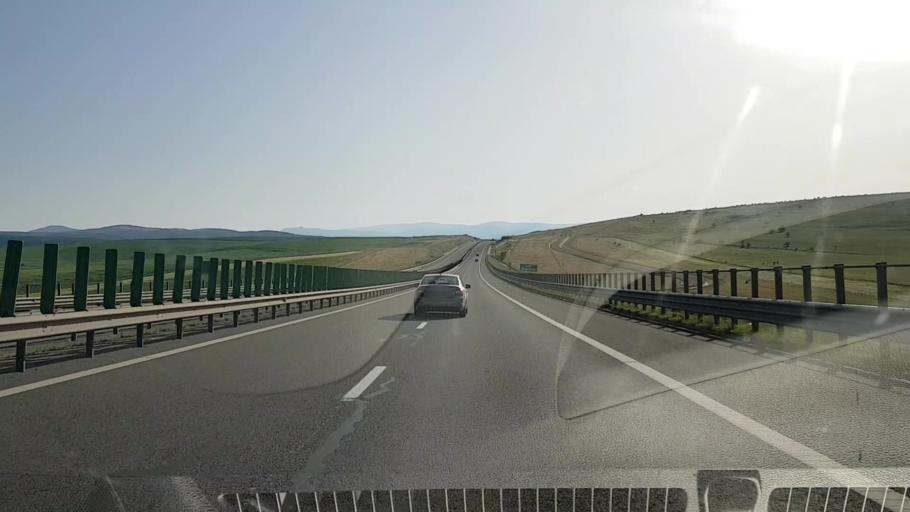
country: RO
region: Cluj
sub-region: Comuna Tureni
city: Tureni
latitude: 46.6027
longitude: 23.6842
